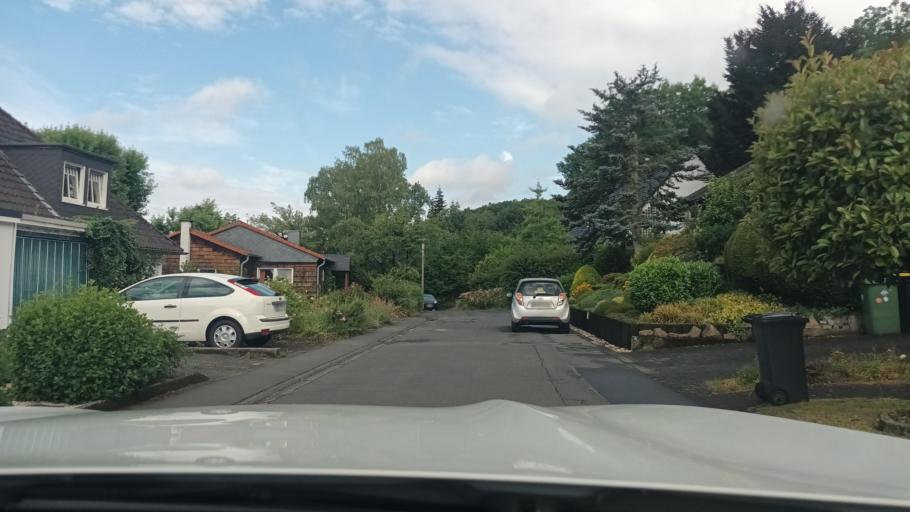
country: DE
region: North Rhine-Westphalia
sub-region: Regierungsbezirk Koln
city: Hennef
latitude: 50.7833
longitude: 7.2961
